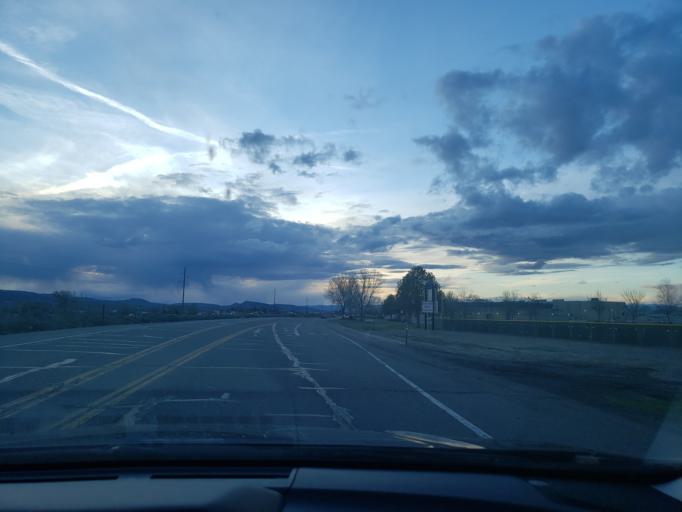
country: US
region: Colorado
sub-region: Mesa County
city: Fruita
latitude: 39.1460
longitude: -108.7144
